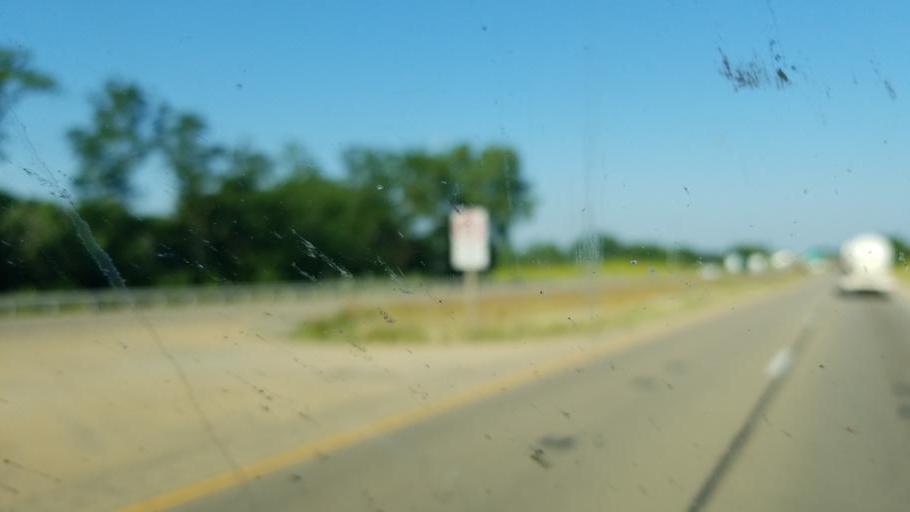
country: US
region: Illinois
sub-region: LaSalle County
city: Deer Park
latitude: 41.3680
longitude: -89.0223
